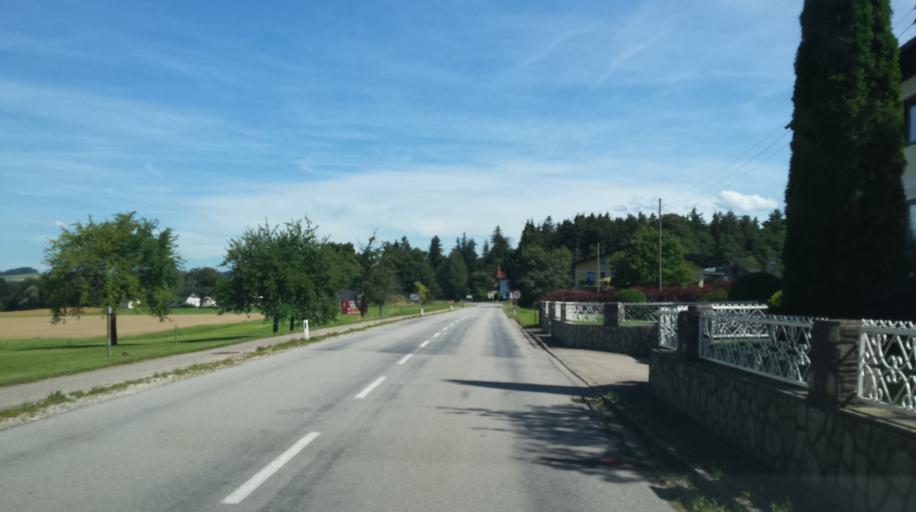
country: AT
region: Upper Austria
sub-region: Politischer Bezirk Vocklabruck
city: Sankt Georgen im Attergau
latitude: 47.9460
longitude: 13.4587
